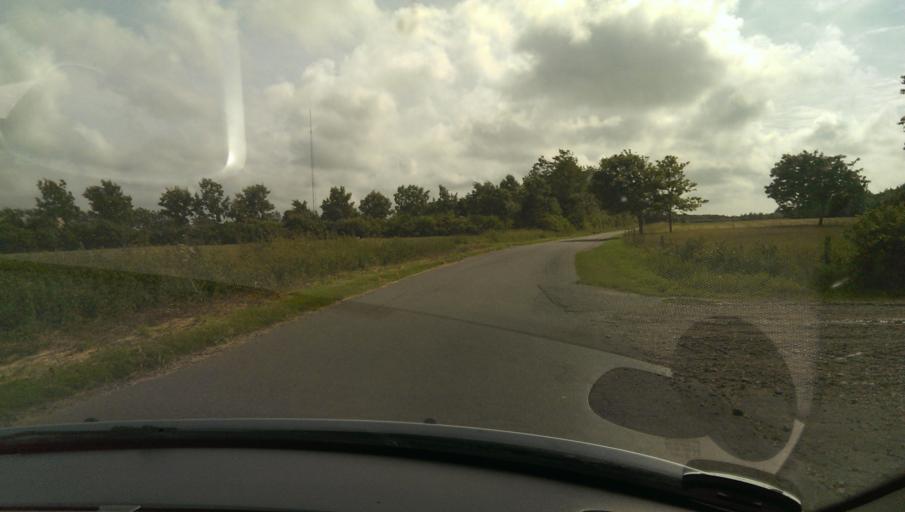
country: DK
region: Central Jutland
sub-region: Holstebro Kommune
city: Ulfborg
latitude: 56.2772
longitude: 8.2712
